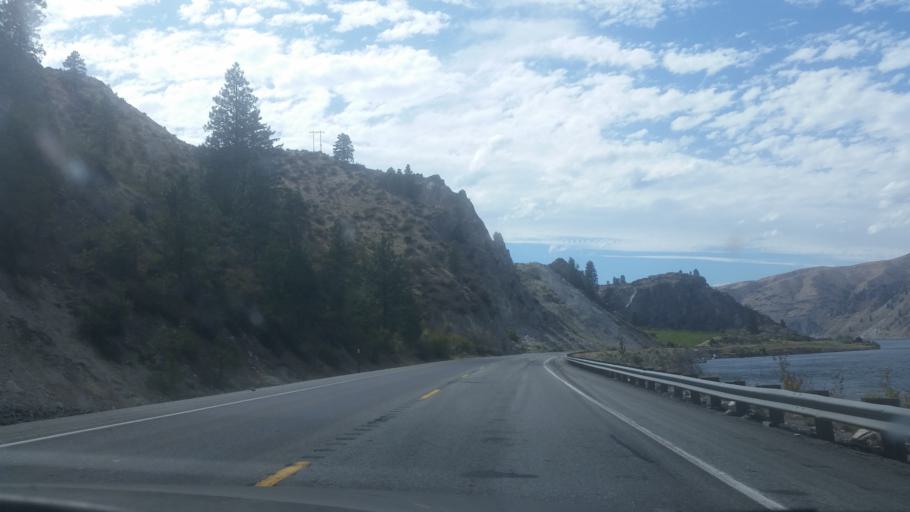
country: US
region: Washington
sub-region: Chelan County
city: Chelan
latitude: 47.7618
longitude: -120.0931
